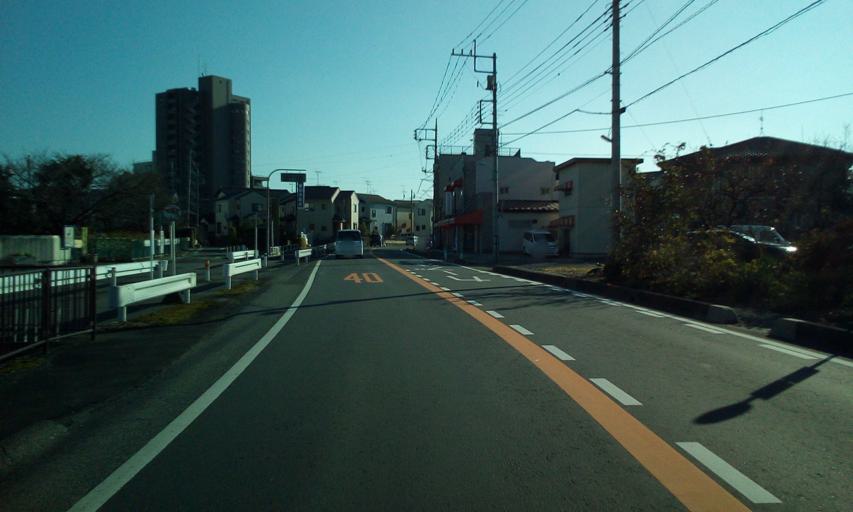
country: JP
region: Chiba
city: Nagareyama
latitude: 35.8618
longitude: 139.8876
